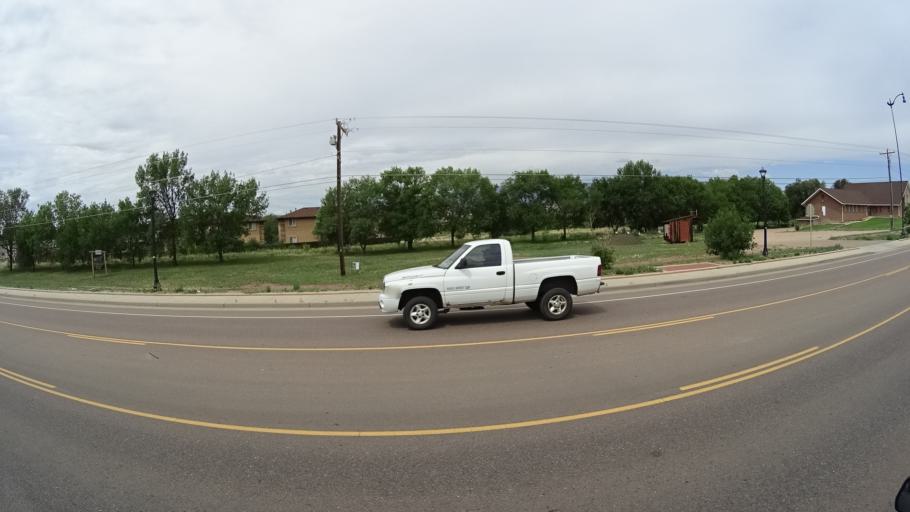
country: US
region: Colorado
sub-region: El Paso County
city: Fountain
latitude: 38.6958
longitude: -104.7051
